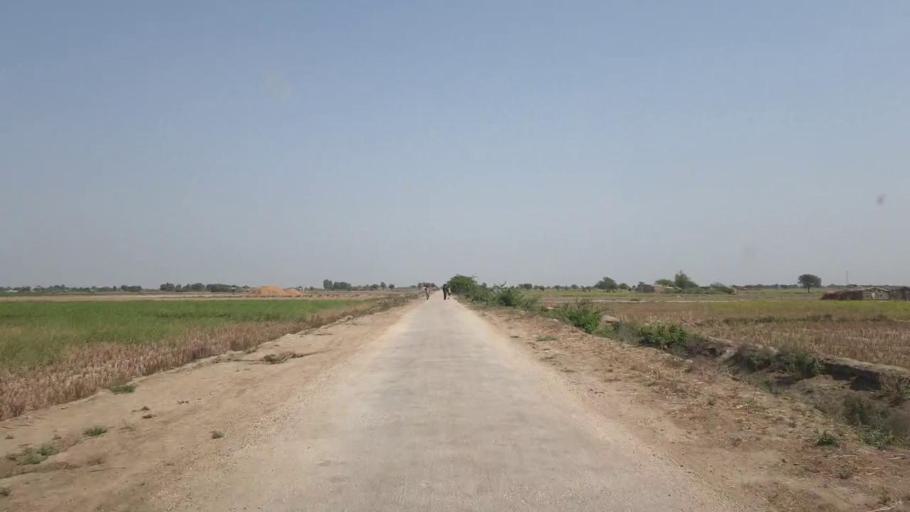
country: PK
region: Sindh
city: Jati
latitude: 24.4774
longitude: 68.5590
